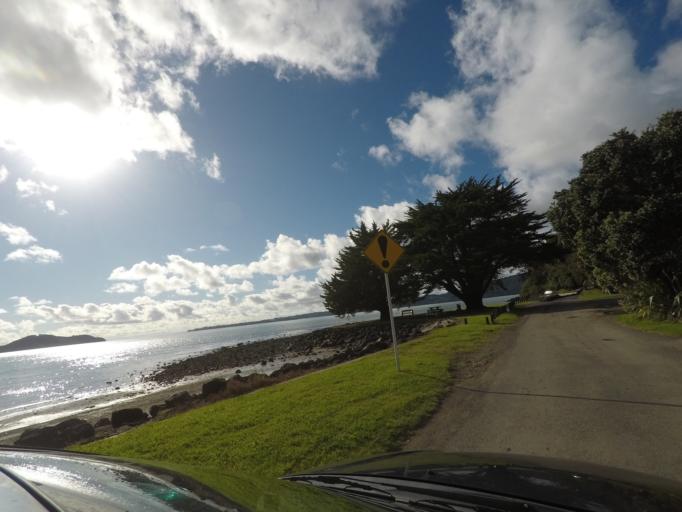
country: NZ
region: Auckland
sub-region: Auckland
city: Titirangi
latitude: -37.0160
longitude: 174.5582
